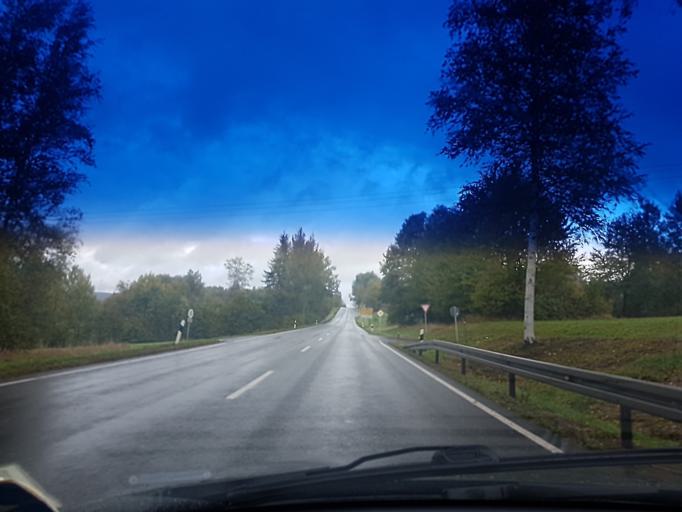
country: DE
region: Bavaria
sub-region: Upper Franconia
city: Bad Alexandersbad
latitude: 50.0169
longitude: 11.9920
